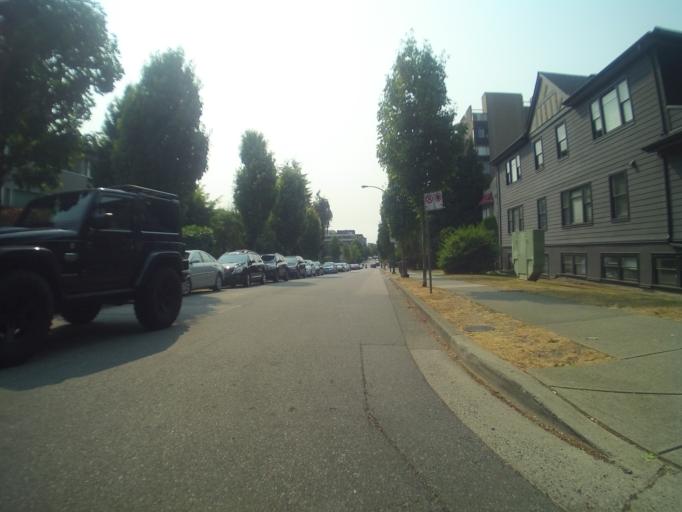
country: CA
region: British Columbia
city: Vancouver
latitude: 49.2626
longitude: -123.1337
